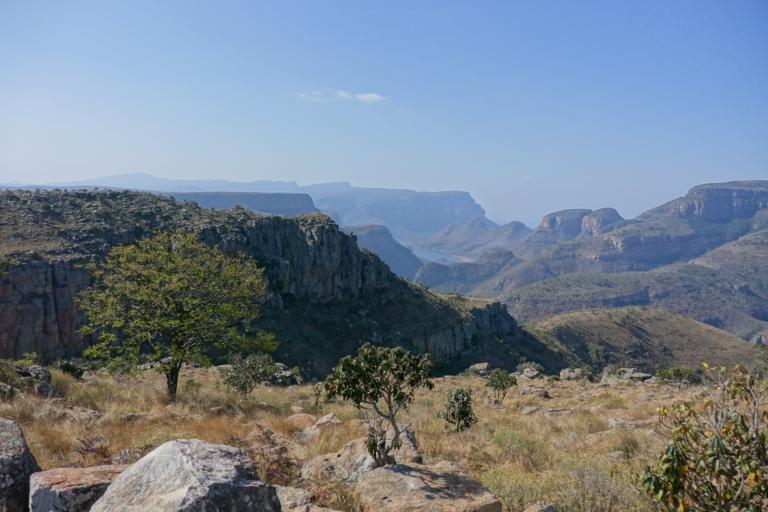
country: ZA
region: Limpopo
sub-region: Mopani District Municipality
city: Hoedspruit
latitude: -24.6049
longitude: 30.8142
